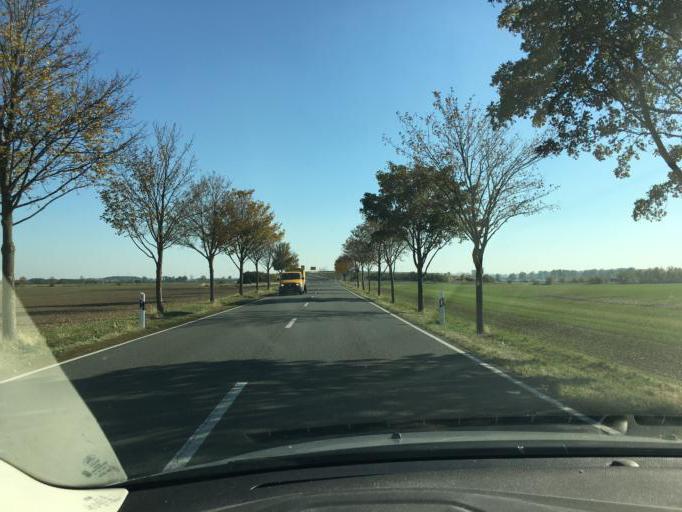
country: DE
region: Saxony-Anhalt
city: Wolmirsleben
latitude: 52.0177
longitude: 11.5020
